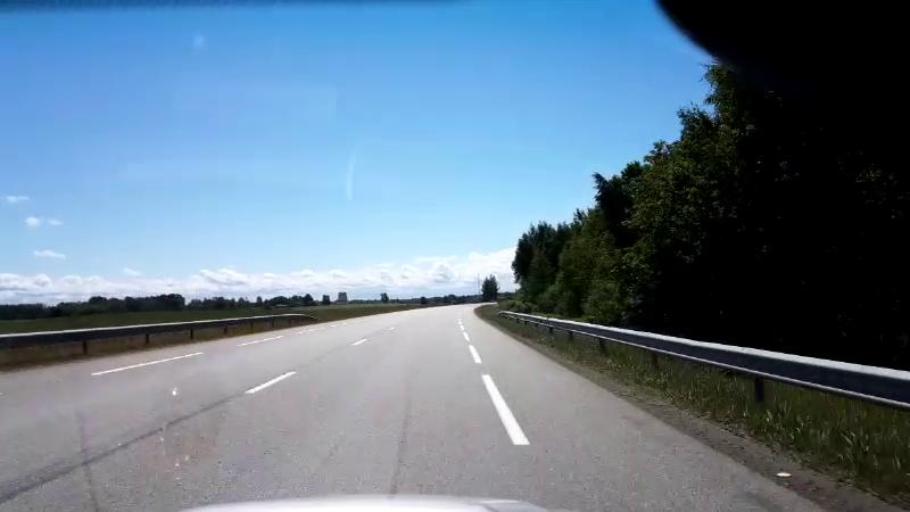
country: LV
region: Saulkrastu
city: Saulkrasti
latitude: 57.4098
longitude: 24.4322
